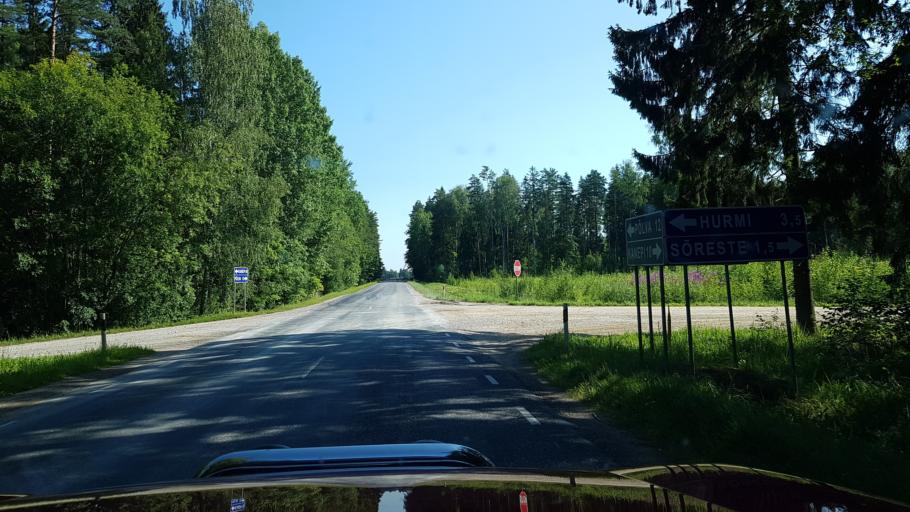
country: EE
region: Polvamaa
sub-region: Polva linn
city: Polva
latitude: 57.9937
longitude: 26.9066
